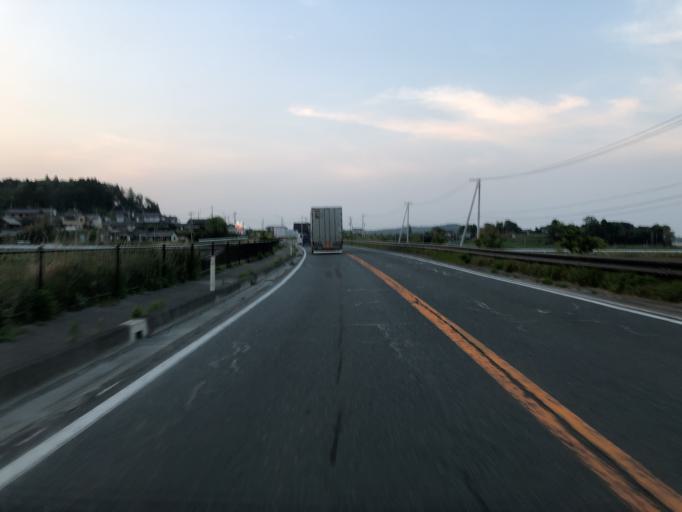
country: JP
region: Fukushima
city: Namie
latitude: 37.5776
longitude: 141.0097
